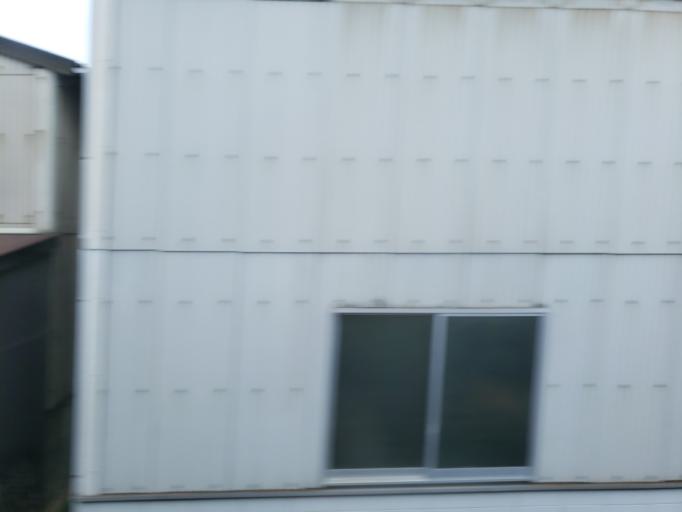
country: JP
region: Hyogo
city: Himeji
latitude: 34.7941
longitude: 134.6896
